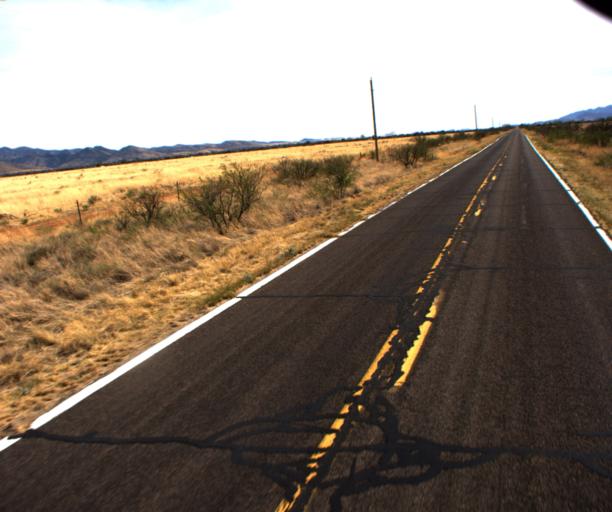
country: US
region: Arizona
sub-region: Cochise County
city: Willcox
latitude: 31.9037
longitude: -109.4914
